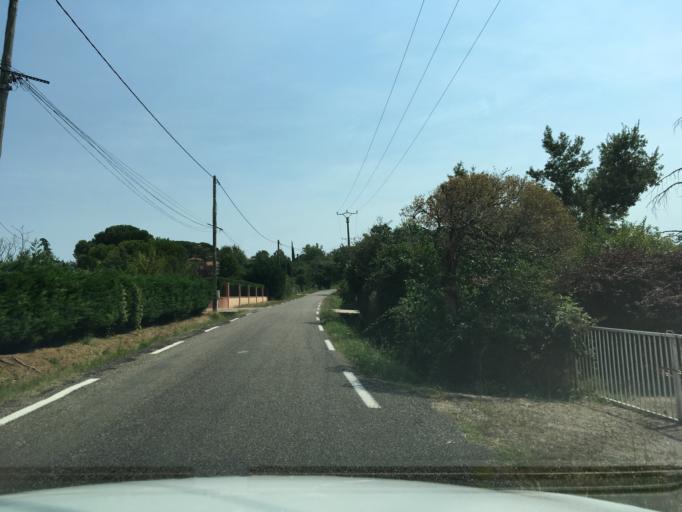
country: FR
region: Midi-Pyrenees
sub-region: Departement du Tarn-et-Garonne
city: Corbarieu
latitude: 43.9712
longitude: 1.3823
